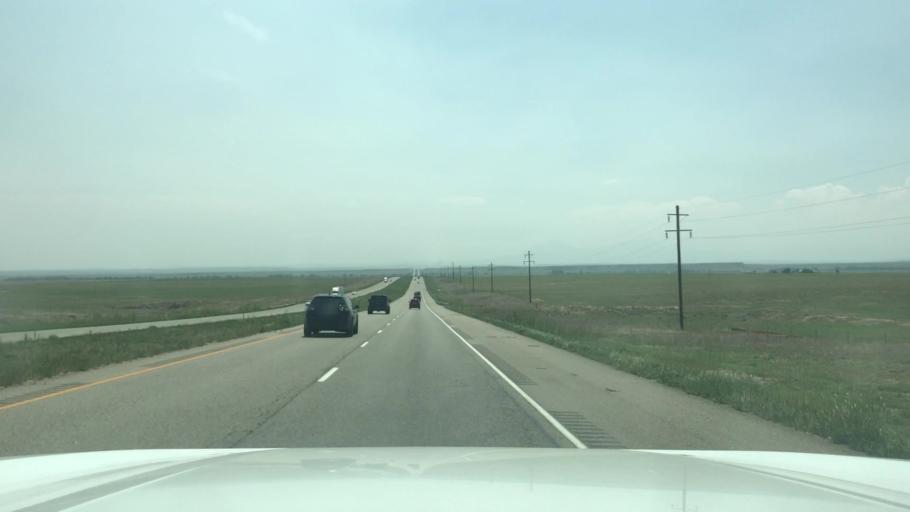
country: US
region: Colorado
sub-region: Pueblo County
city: Colorado City
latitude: 37.8838
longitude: -104.8295
